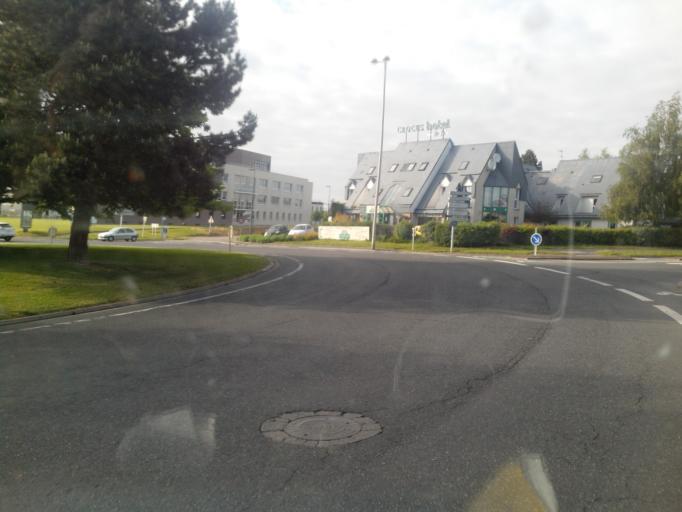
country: FR
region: Lower Normandy
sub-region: Departement du Calvados
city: Saint-Contest
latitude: 49.2028
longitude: -0.3911
